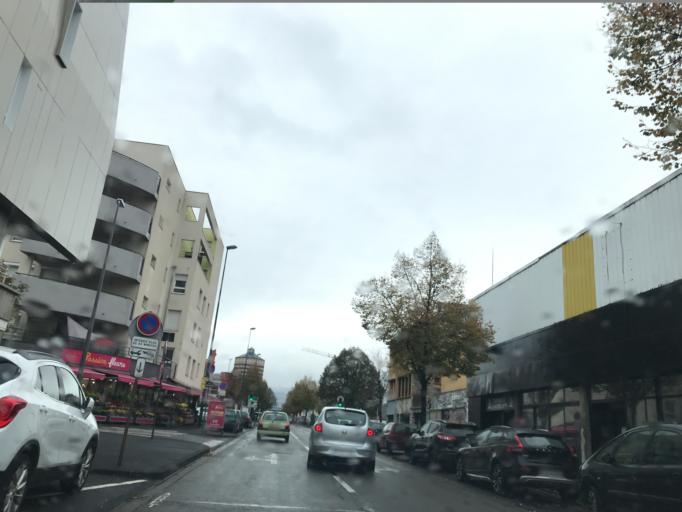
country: FR
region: Auvergne
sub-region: Departement du Puy-de-Dome
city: Clermont-Ferrand
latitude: 45.7806
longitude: 3.1103
